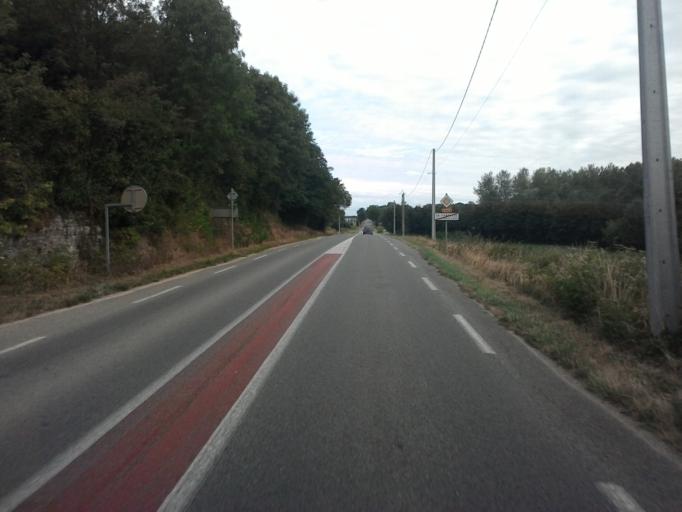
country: FR
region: Rhone-Alpes
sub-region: Departement de l'Ain
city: Saint-Martin-du-Mont
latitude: 46.0831
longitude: 5.3185
